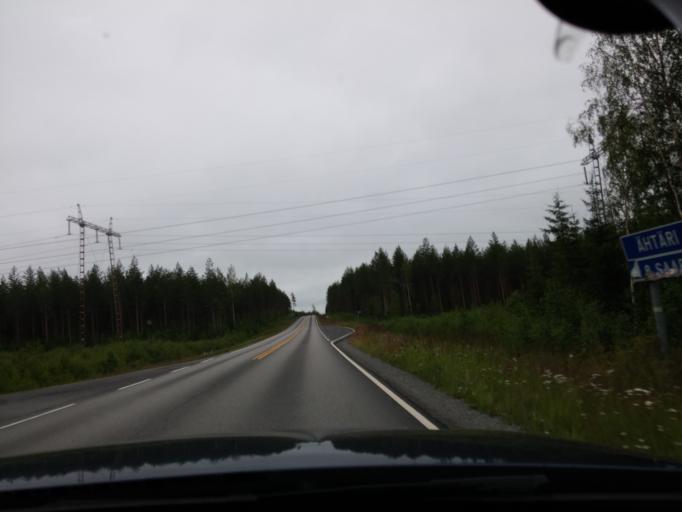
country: FI
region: Central Finland
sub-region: Saarijaervi-Viitasaari
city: Saarijaervi
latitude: 62.6793
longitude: 25.1752
